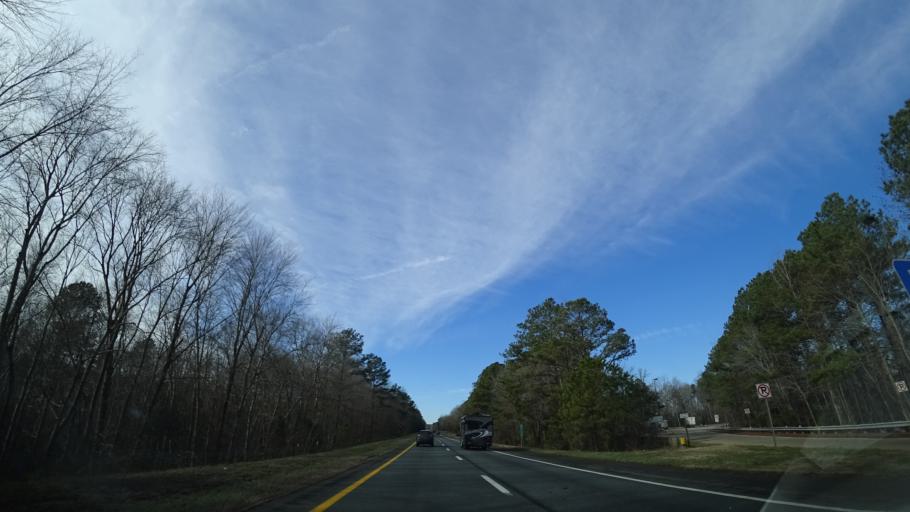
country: US
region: Virginia
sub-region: New Kent County
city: New Kent
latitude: 37.4964
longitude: -77.0399
